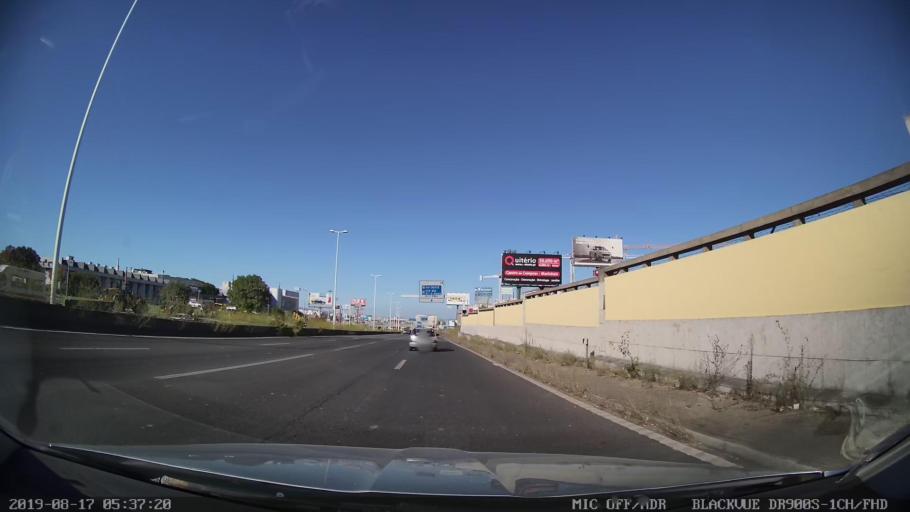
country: PT
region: Lisbon
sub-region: Loures
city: Sacavem
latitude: 38.7855
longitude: -9.1193
